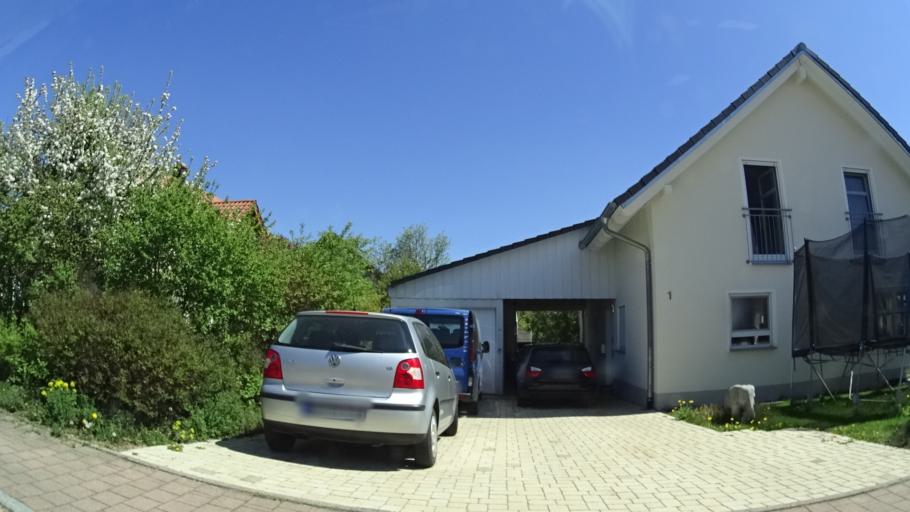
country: DE
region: Baden-Wuerttemberg
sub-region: Freiburg Region
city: Zimmern ob Rottweil
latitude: 48.1715
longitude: 8.6007
